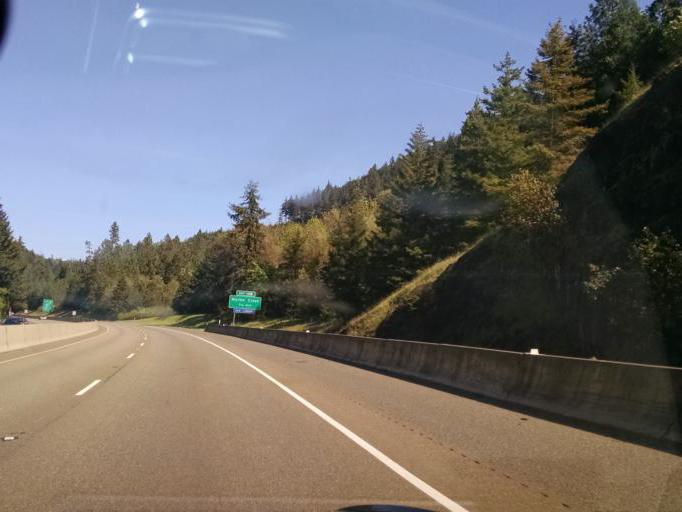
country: US
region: Oregon
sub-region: Douglas County
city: Myrtle Creek
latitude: 43.0297
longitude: -123.3153
